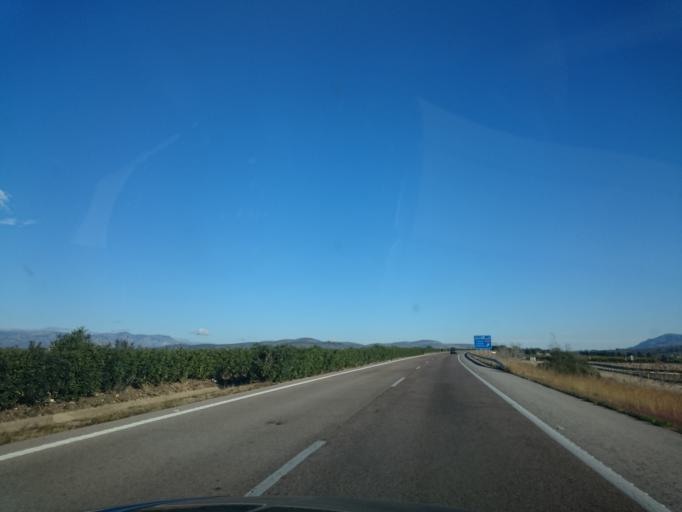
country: ES
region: Catalonia
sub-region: Provincia de Tarragona
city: Ulldecona
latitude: 40.5489
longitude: 0.4211
